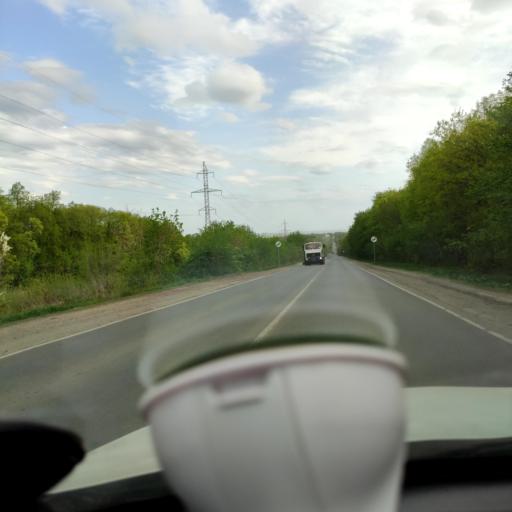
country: RU
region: Samara
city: Novosemeykino
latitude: 53.3296
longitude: 50.2582
